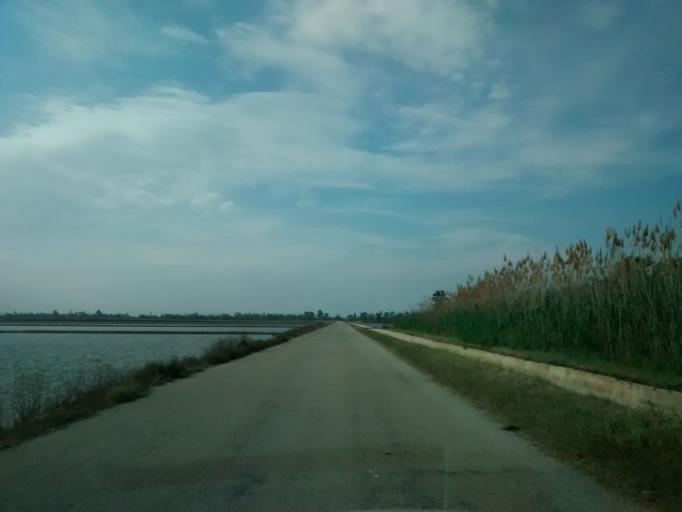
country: ES
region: Catalonia
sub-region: Provincia de Tarragona
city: Deltebre
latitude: 40.7002
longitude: 0.8265
